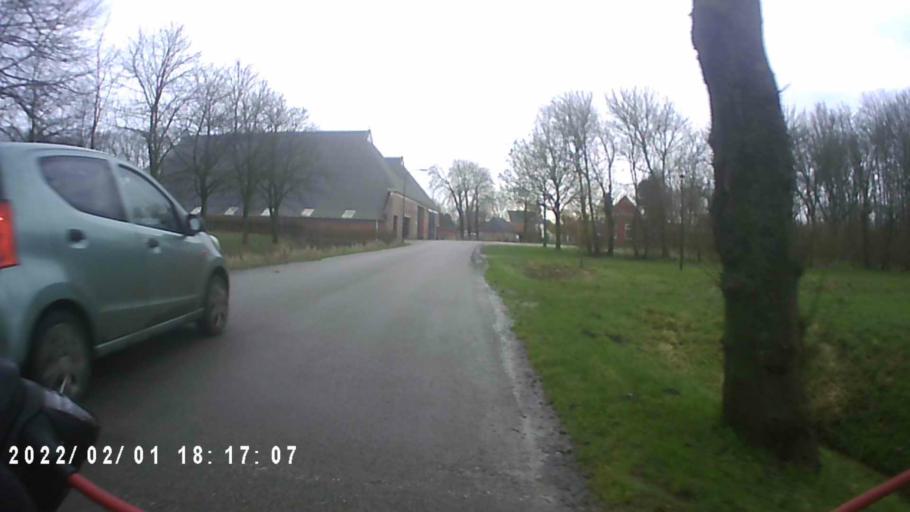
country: NL
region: Groningen
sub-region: Gemeente De Marne
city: Ulrum
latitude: 53.3440
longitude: 6.3314
